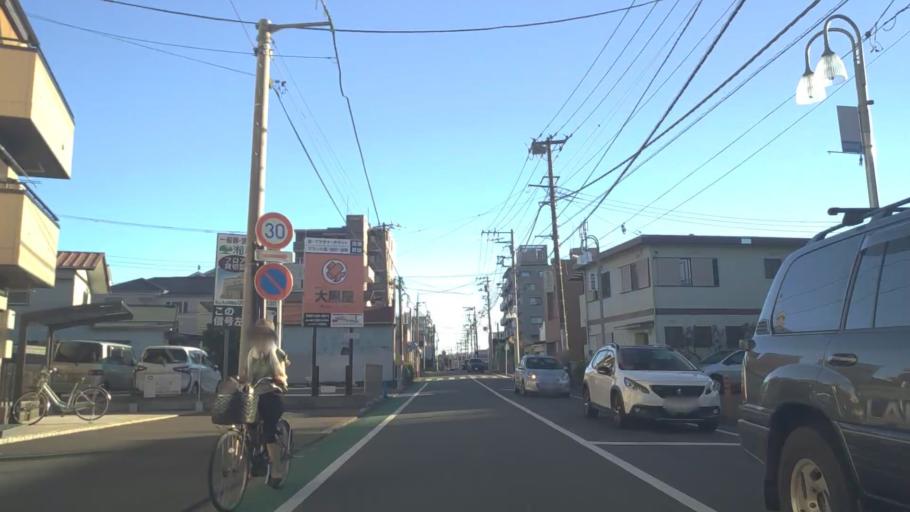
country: JP
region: Kanagawa
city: Chigasaki
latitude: 35.3321
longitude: 139.4147
